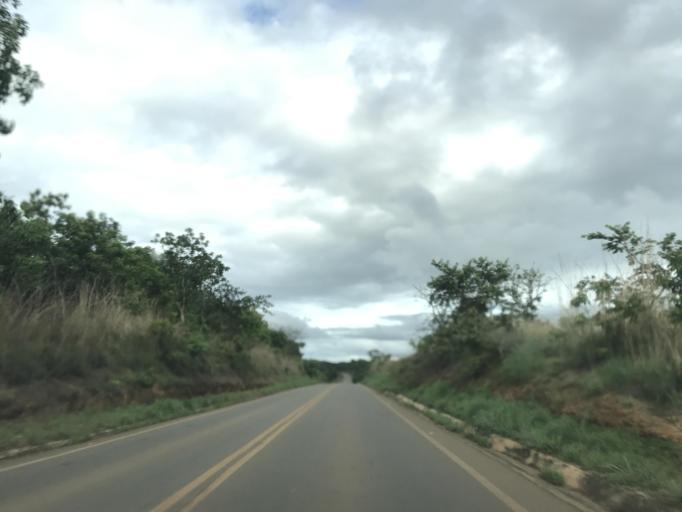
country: BR
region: Goias
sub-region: Vianopolis
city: Vianopolis
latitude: -16.7255
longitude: -48.4216
